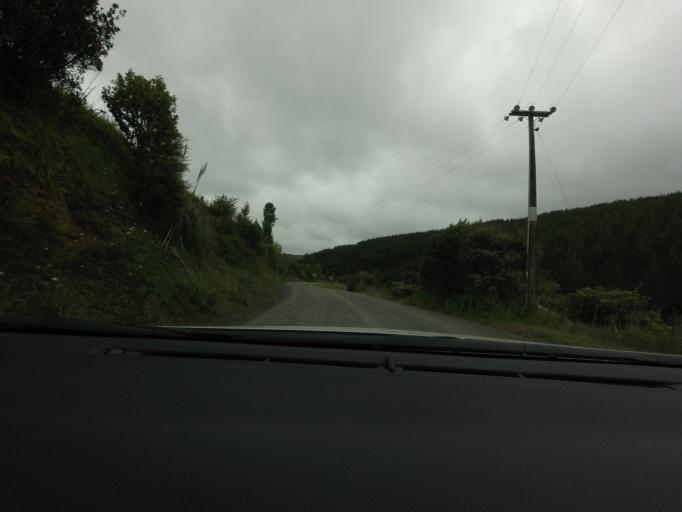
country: NZ
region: Auckland
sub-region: Auckland
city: Warkworth
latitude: -36.4693
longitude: 174.5522
